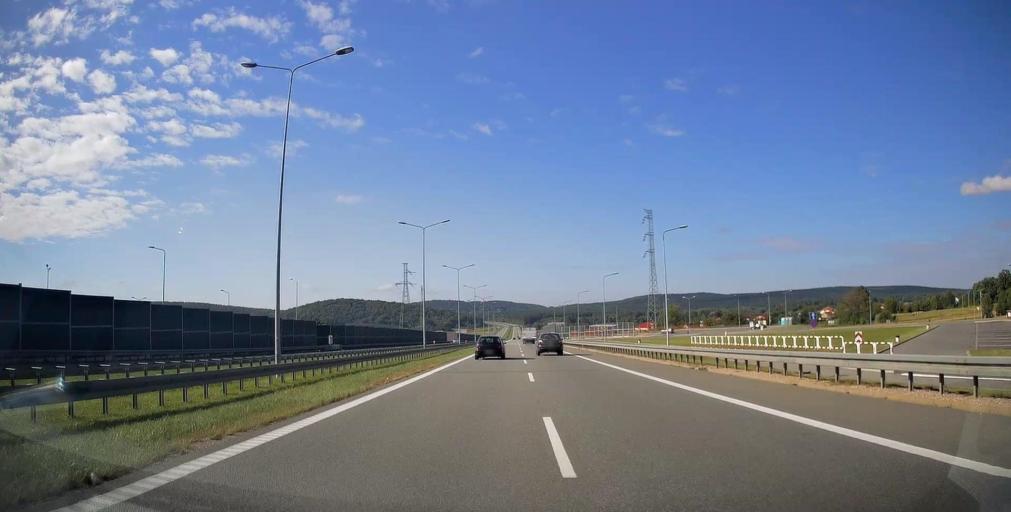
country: PL
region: Swietokrzyskie
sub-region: Powiat kielecki
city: Piekoszow
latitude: 50.8432
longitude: 20.4829
